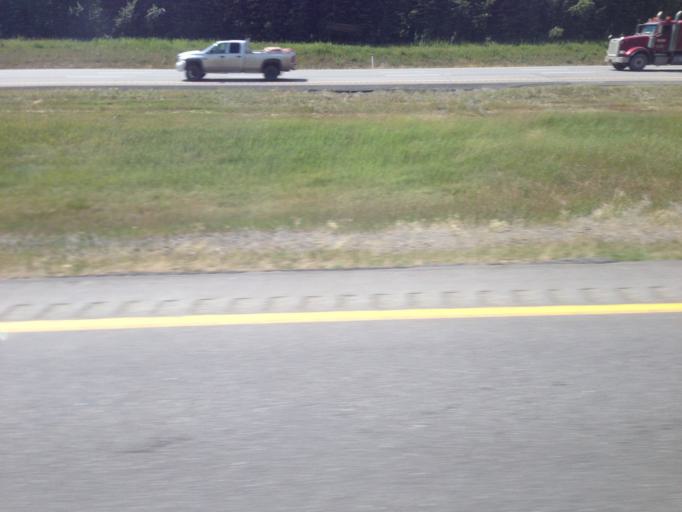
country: CA
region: Alberta
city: Cochrane
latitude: 51.1494
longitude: -114.7382
